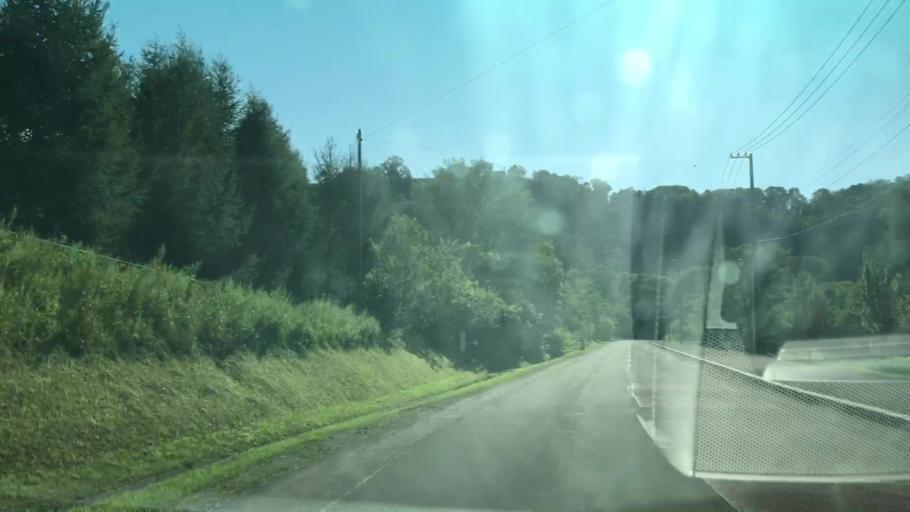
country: JP
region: Hokkaido
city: Date
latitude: 42.5637
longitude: 140.8128
